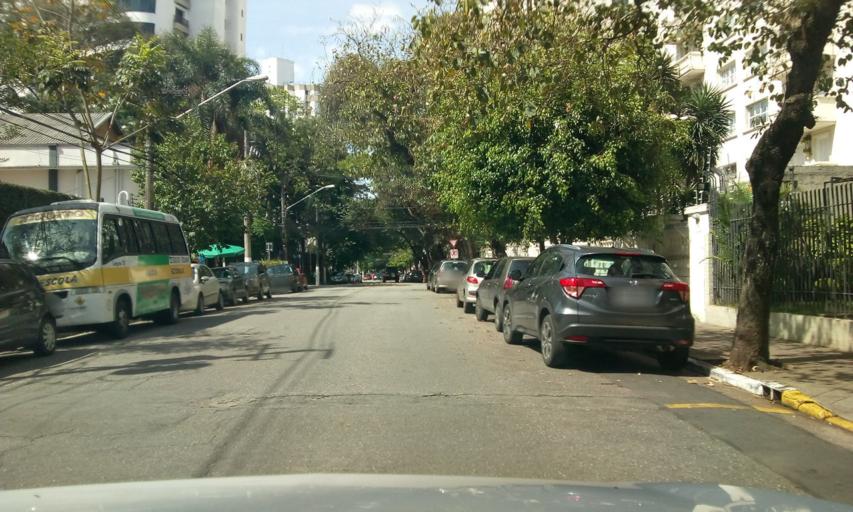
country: BR
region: Sao Paulo
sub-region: Sao Paulo
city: Sao Paulo
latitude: -23.6192
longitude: -46.6784
